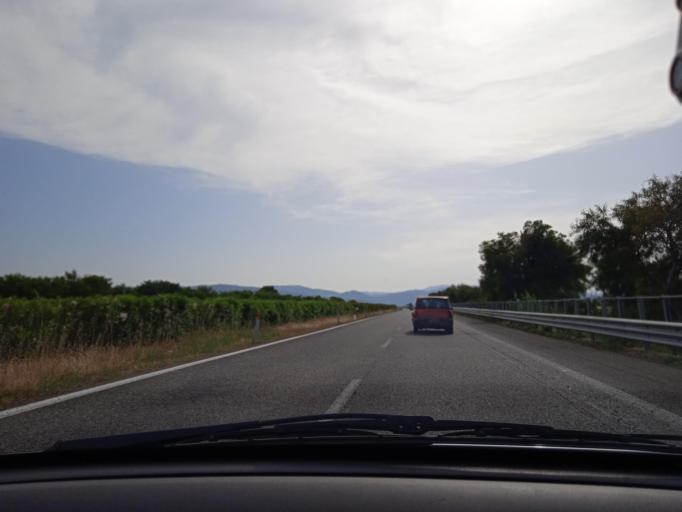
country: IT
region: Sicily
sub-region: Messina
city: Terme
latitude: 38.1343
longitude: 15.1425
